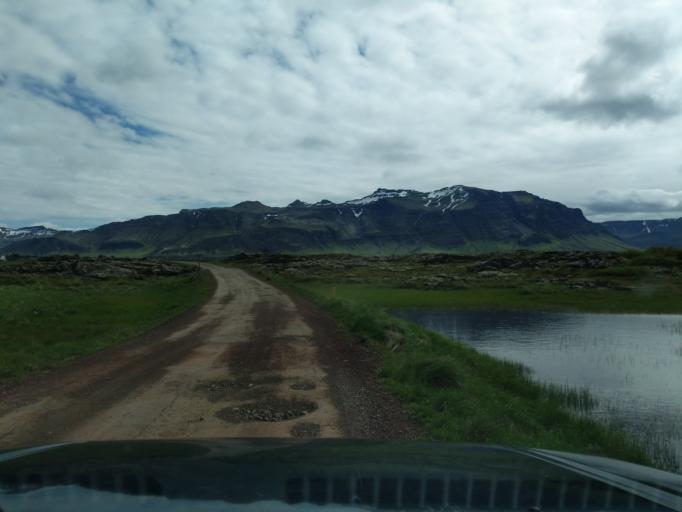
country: IS
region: West
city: Borgarnes
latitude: 64.8323
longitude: -22.2961
